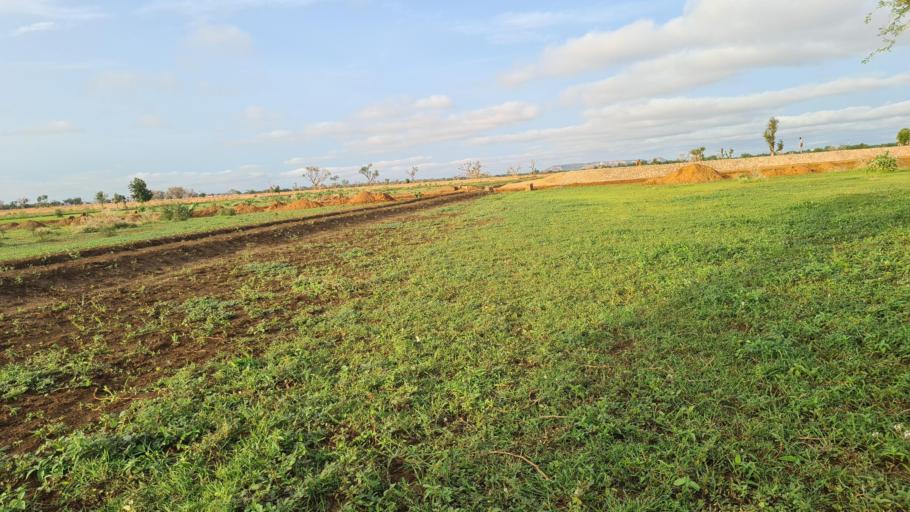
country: NE
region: Tahoua
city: Birni N Konni
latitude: 13.7854
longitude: 5.2314
